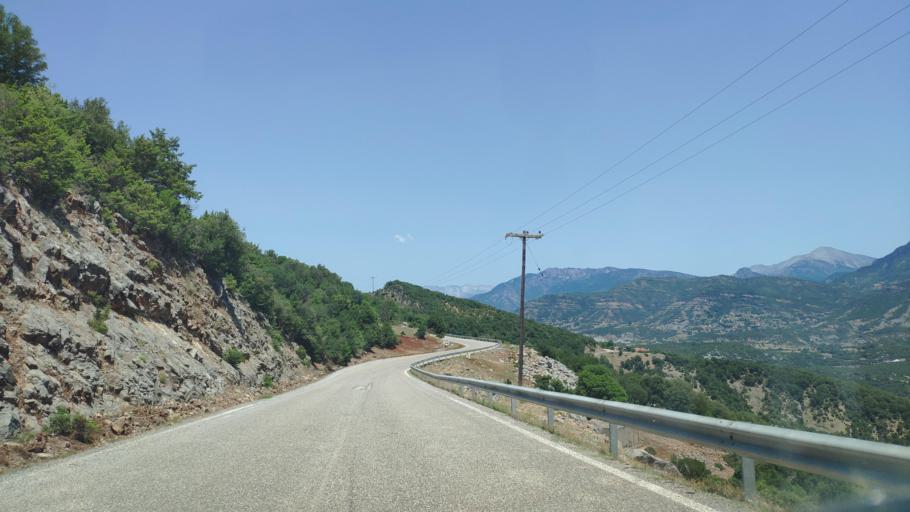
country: GR
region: Central Greece
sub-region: Nomos Evrytanias
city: Kerasochori
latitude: 39.0982
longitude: 21.4123
